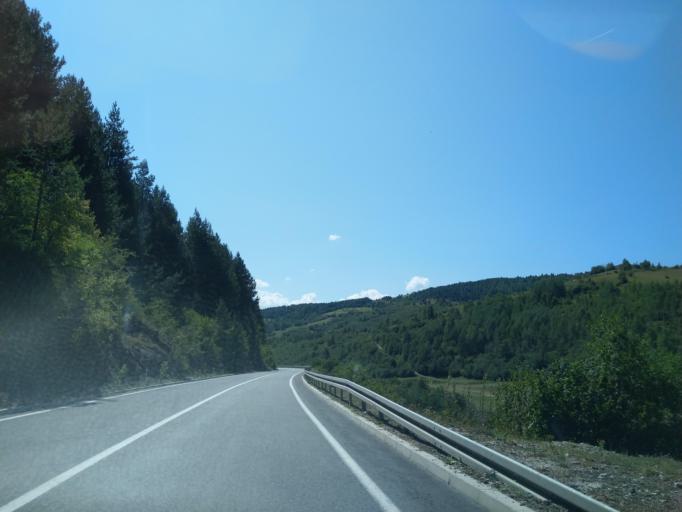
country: RS
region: Central Serbia
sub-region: Zlatiborski Okrug
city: Sjenica
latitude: 43.2903
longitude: 19.9420
